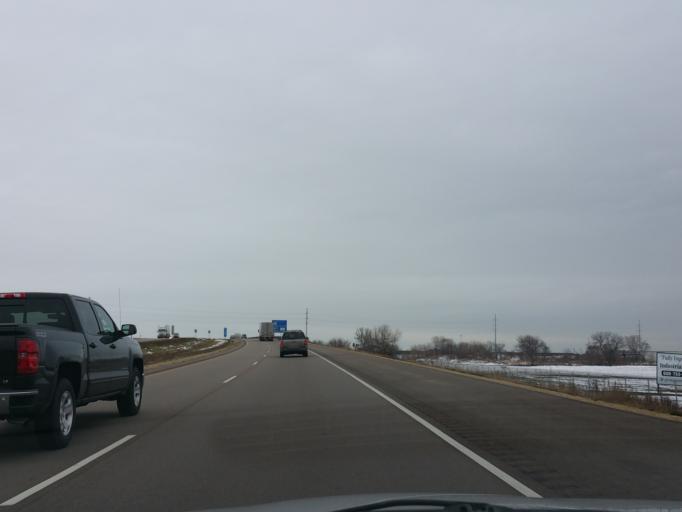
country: US
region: Wisconsin
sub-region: Rock County
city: Janesville
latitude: 42.7322
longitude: -89.0016
